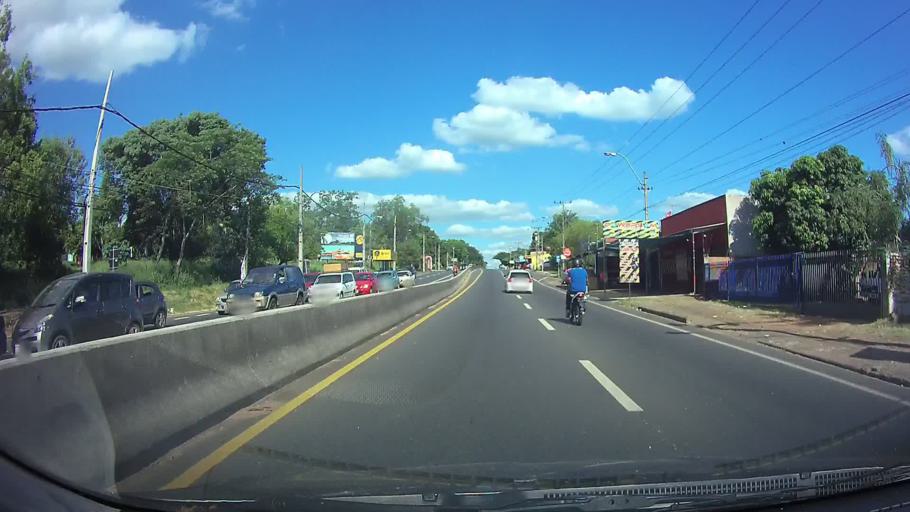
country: PY
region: Central
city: Itaugua
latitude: -25.3963
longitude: -57.3457
